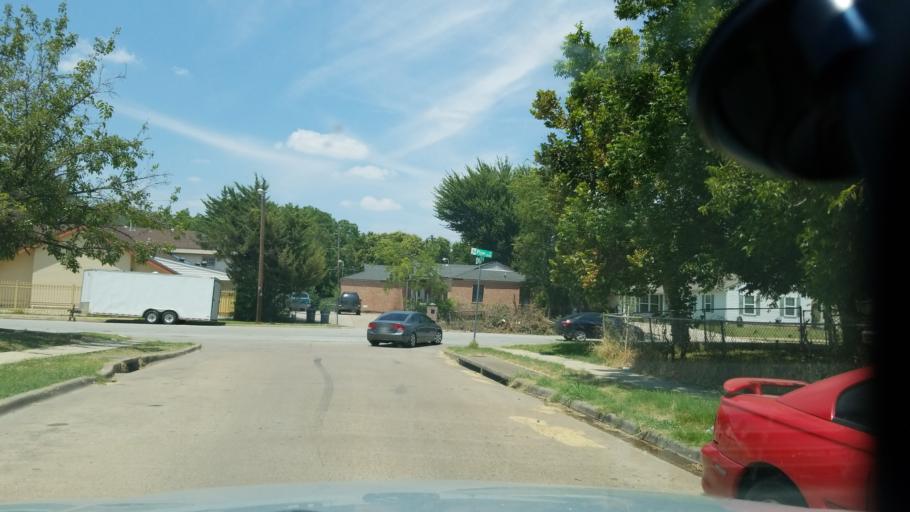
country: US
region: Texas
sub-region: Dallas County
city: Grand Prairie
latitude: 32.7522
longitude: -96.9747
